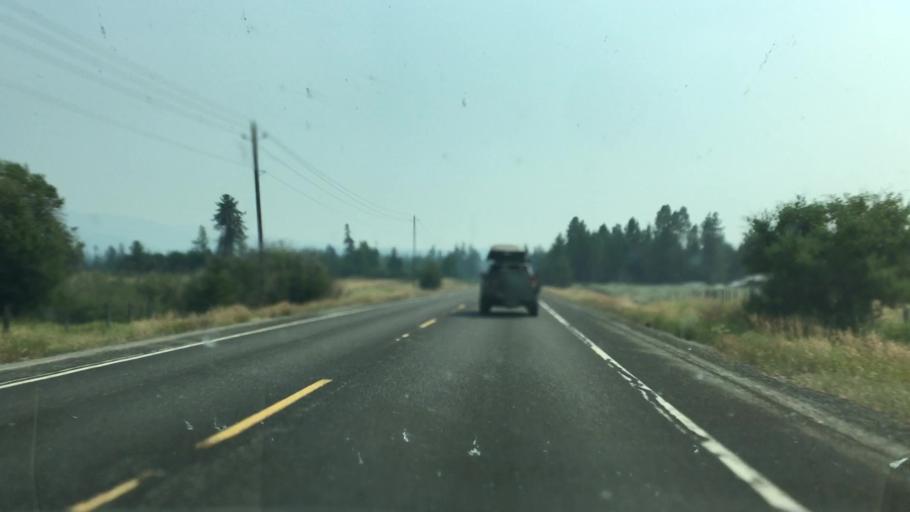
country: US
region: Idaho
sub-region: Valley County
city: Cascade
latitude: 44.4160
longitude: -115.9997
